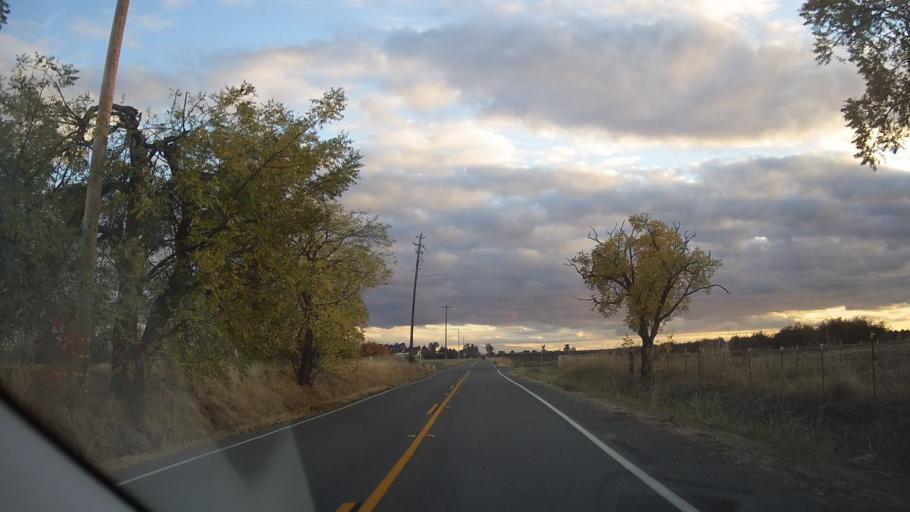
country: US
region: California
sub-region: Solano County
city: Hartley
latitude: 38.3961
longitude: -121.9059
